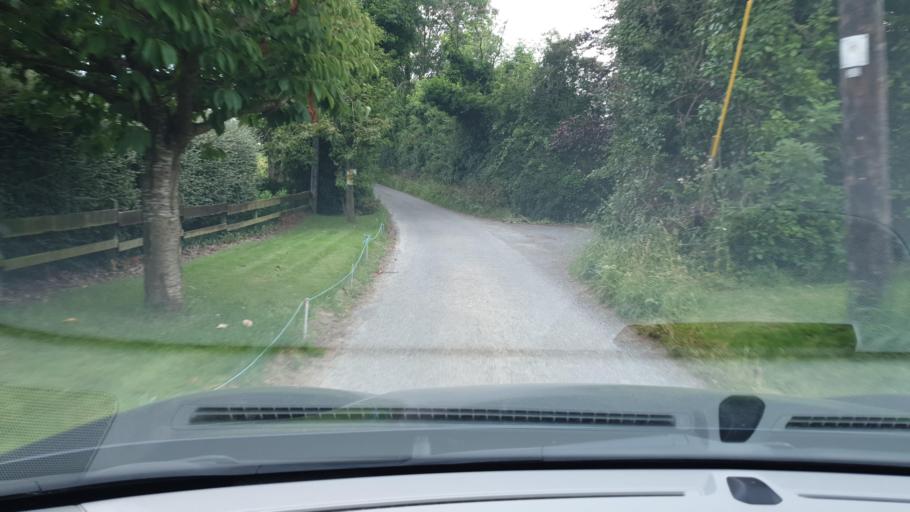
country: IE
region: Leinster
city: Lusk
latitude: 53.5377
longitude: -6.1553
